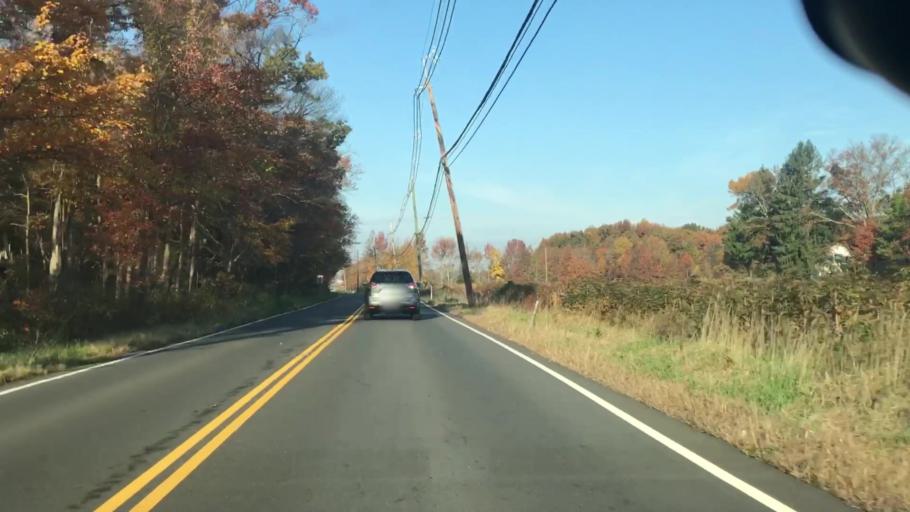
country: US
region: New Jersey
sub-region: Middlesex County
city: Cranbury
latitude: 40.3316
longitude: -74.5192
